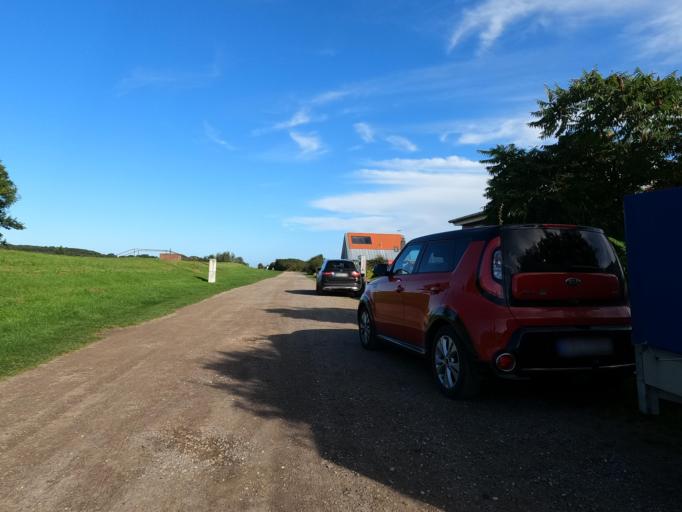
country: DE
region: Schleswig-Holstein
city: Dahme
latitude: 54.2750
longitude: 11.0830
